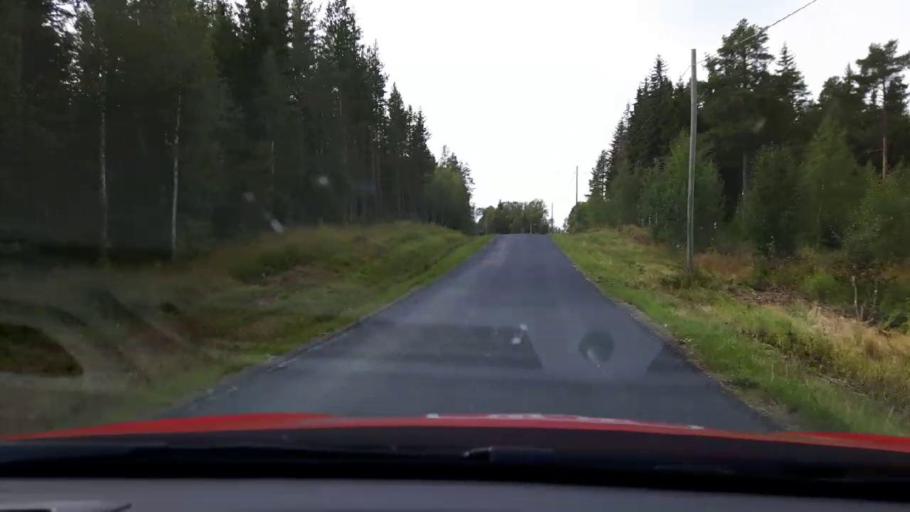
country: SE
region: Jaemtland
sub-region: Krokoms Kommun
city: Valla
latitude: 63.2710
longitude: 13.8588
